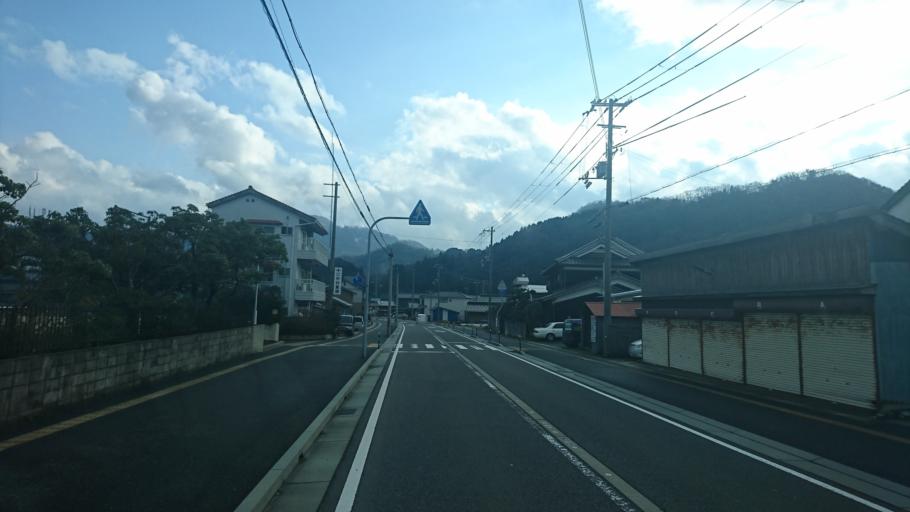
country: JP
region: Tottori
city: Tottori
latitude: 35.6265
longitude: 134.4453
